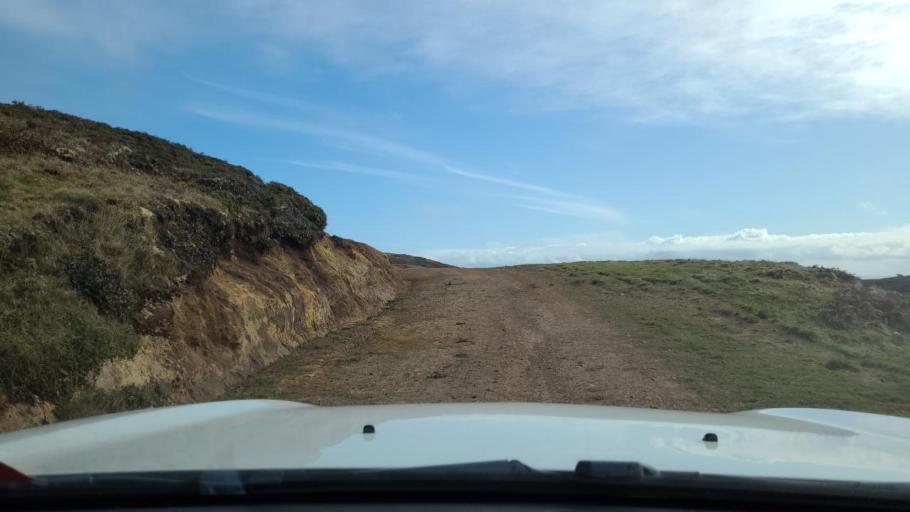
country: NZ
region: Chatham Islands
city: Waitangi
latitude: -44.0577
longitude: -176.6342
